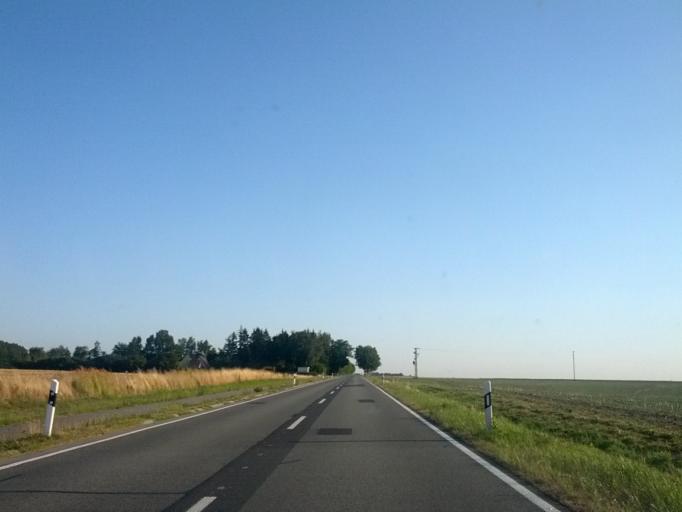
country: DE
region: Mecklenburg-Vorpommern
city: Brandshagen
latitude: 54.1705
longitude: 13.1797
